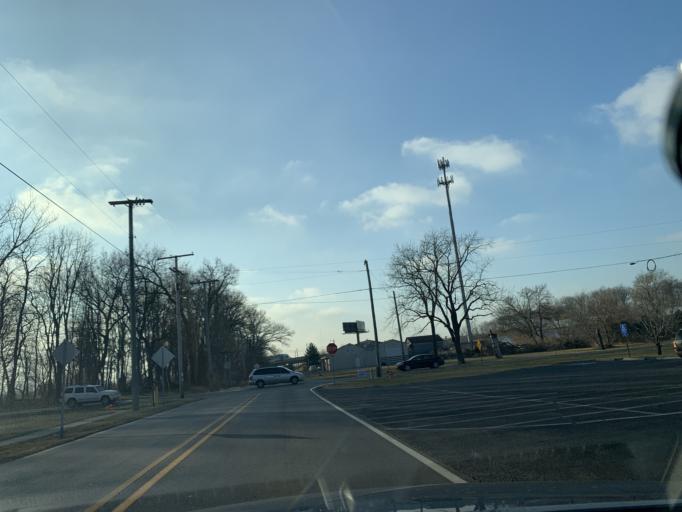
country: US
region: Indiana
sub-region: Porter County
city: Portage
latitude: 41.5764
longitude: -87.1534
